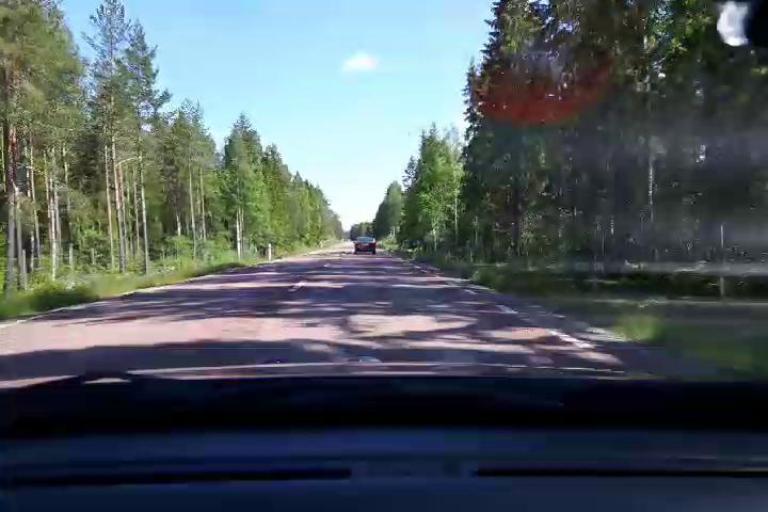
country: SE
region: Gaevleborg
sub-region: Hudiksvalls Kommun
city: Delsbo
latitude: 61.7938
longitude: 16.5802
